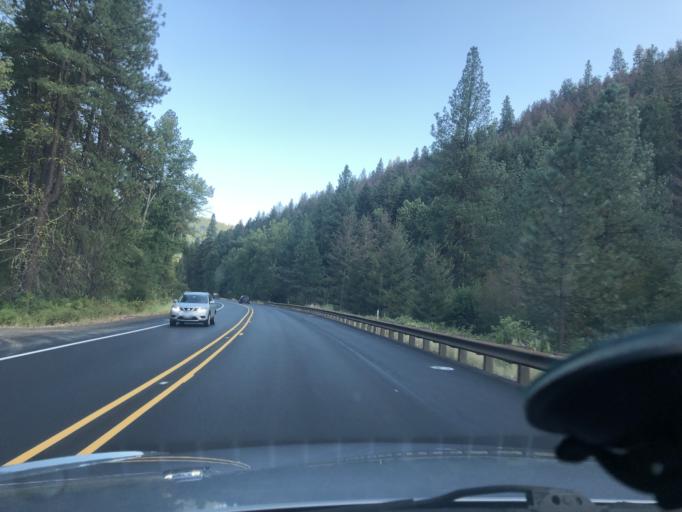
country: US
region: Washington
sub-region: Kittitas County
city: Cle Elum
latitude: 47.2563
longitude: -120.6956
